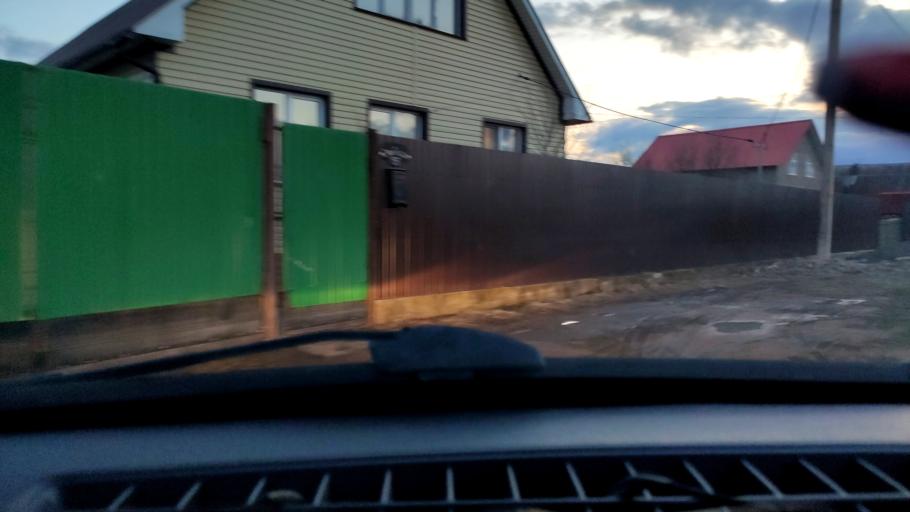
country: RU
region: Bashkortostan
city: Ulukulevo
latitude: 54.4203
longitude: 56.3390
